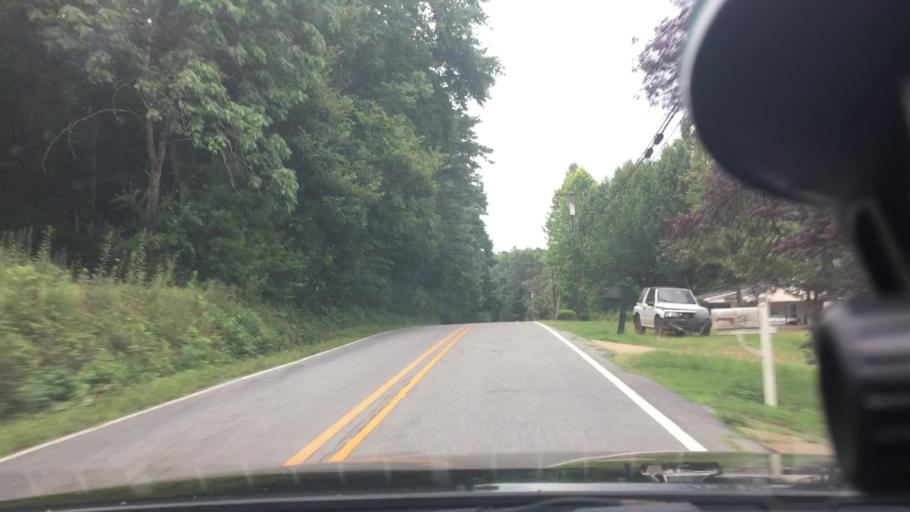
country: US
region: North Carolina
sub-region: McDowell County
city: West Marion
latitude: 35.6584
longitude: -82.0168
